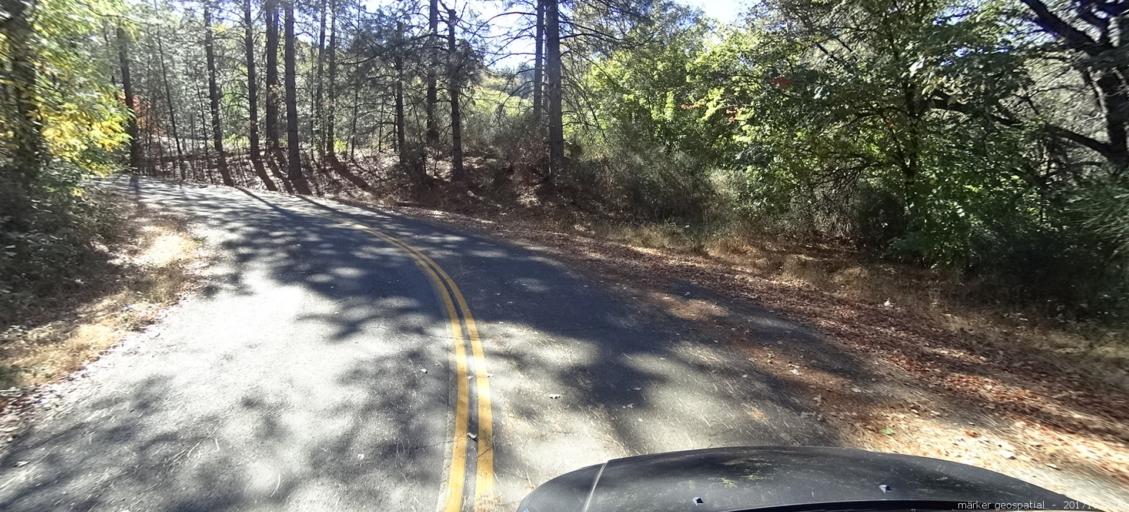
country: US
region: California
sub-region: Shasta County
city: Central Valley (historical)
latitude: 40.9226
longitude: -122.4038
